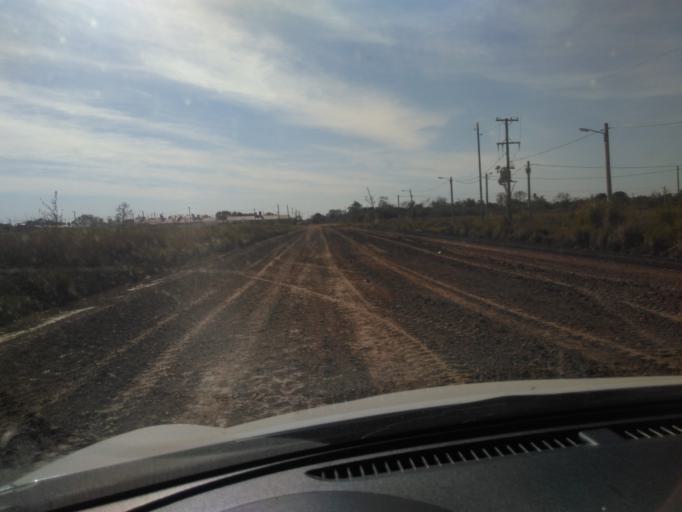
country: AR
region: Chaco
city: Fontana
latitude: -27.4051
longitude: -58.9779
